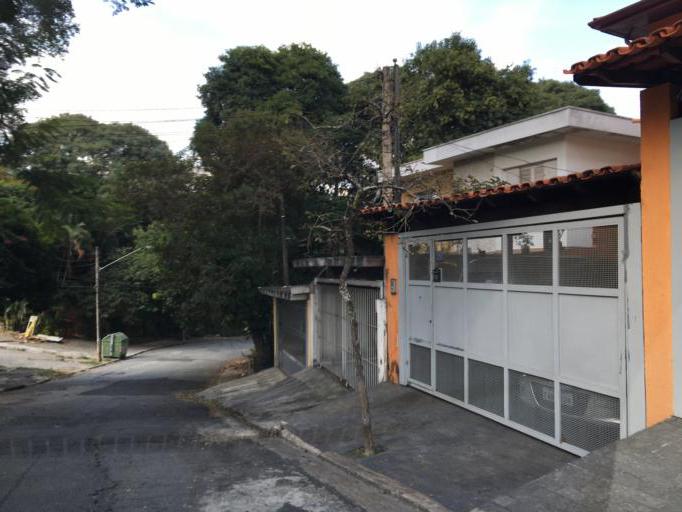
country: BR
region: Sao Paulo
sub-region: Osasco
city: Osasco
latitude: -23.5763
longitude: -46.7358
